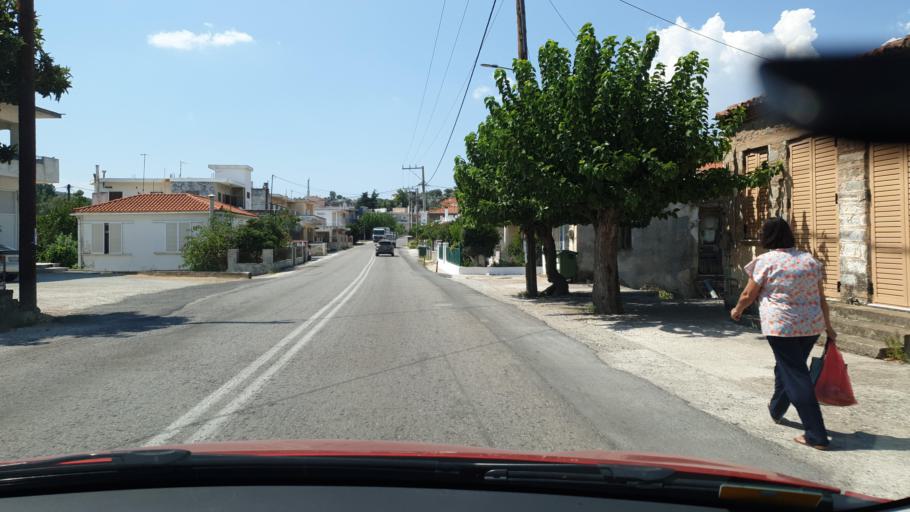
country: GR
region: Central Greece
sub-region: Nomos Evvoias
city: Aliveri
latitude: 38.3921
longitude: 24.0939
